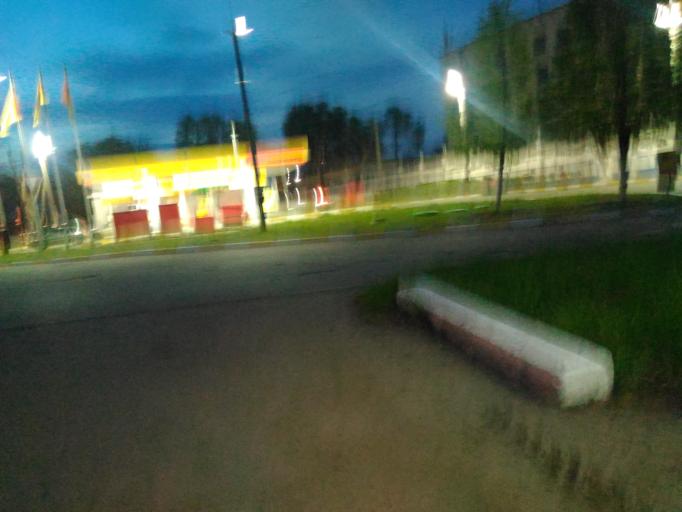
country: RU
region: Ulyanovsk
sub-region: Ulyanovskiy Rayon
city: Ulyanovsk
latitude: 54.2782
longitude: 48.3441
